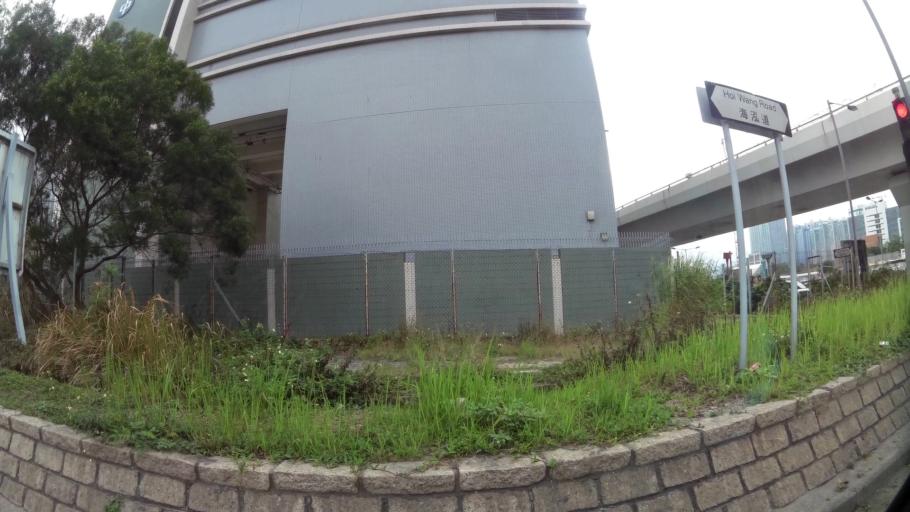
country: HK
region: Sham Shui Po
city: Sham Shui Po
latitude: 22.3118
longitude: 114.1646
